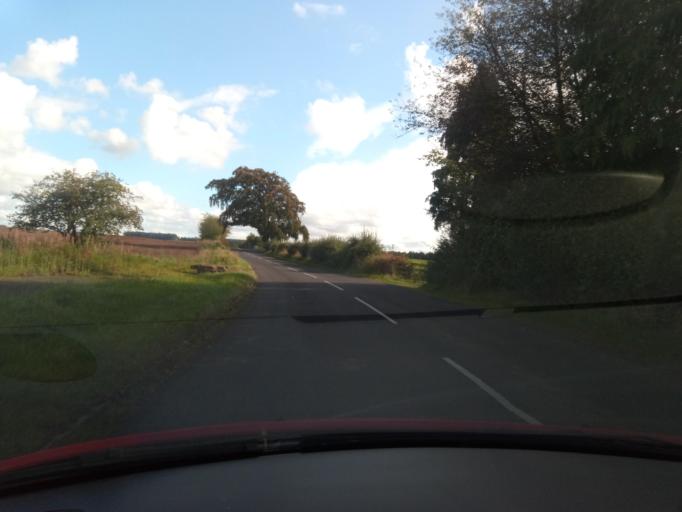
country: GB
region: Scotland
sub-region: The Scottish Borders
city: Kelso
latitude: 55.5745
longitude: -2.3971
